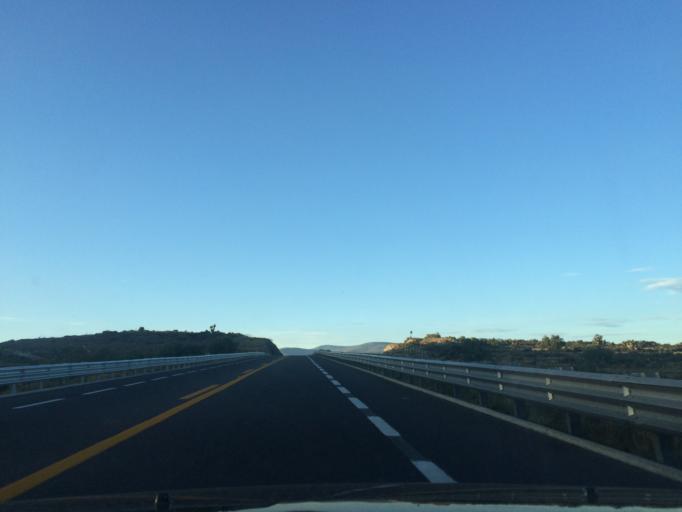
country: MX
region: Puebla
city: Cuacnopalan
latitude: 18.8067
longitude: -97.4903
